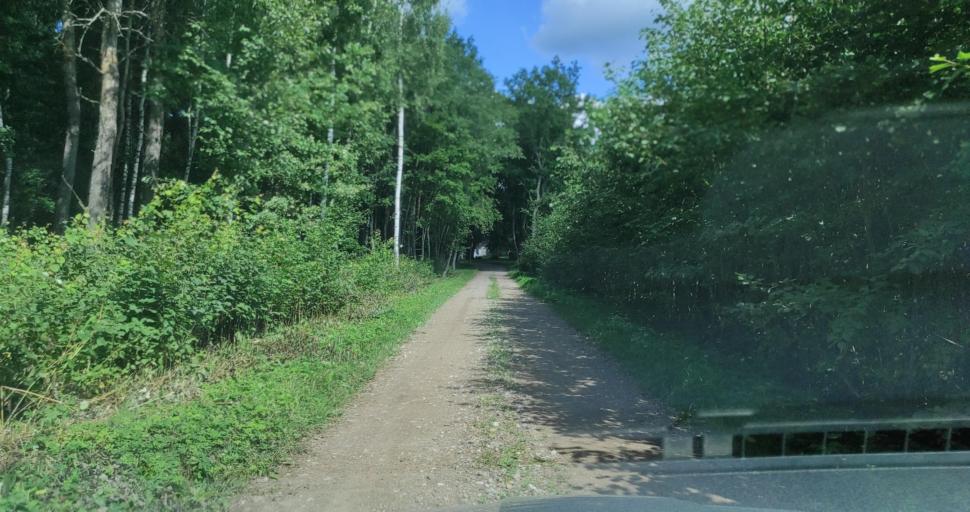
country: LV
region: Alsunga
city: Alsunga
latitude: 57.0239
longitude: 21.7046
